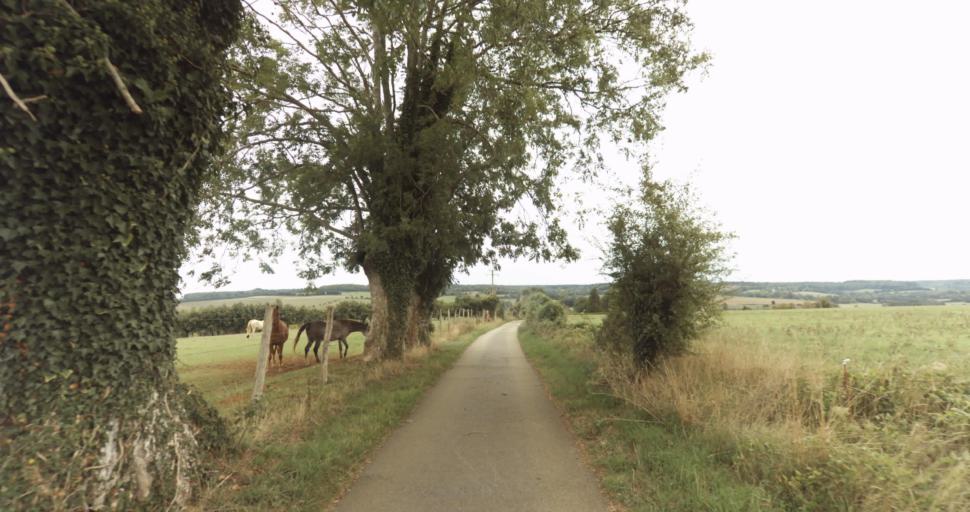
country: FR
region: Lower Normandy
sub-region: Departement de l'Orne
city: Gace
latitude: 48.7620
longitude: 0.3230
